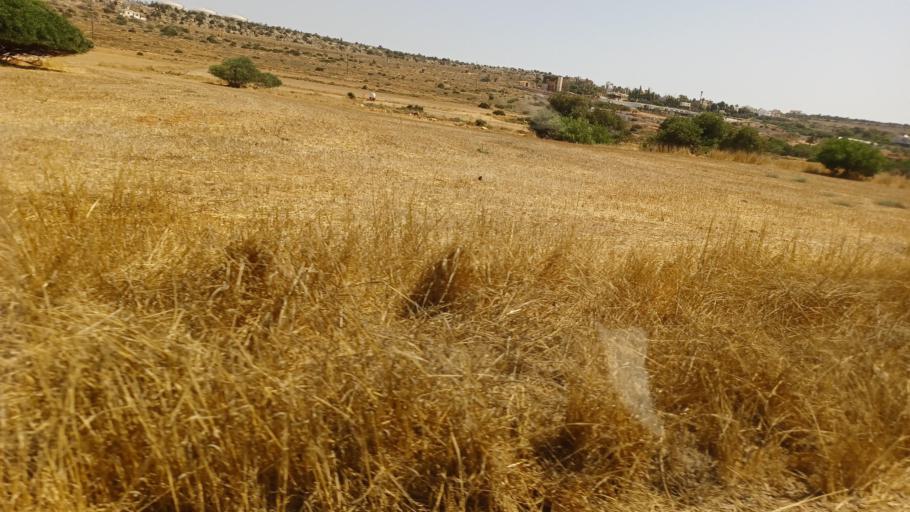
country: CY
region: Ammochostos
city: Ayia Napa
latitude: 35.0039
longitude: 33.9740
